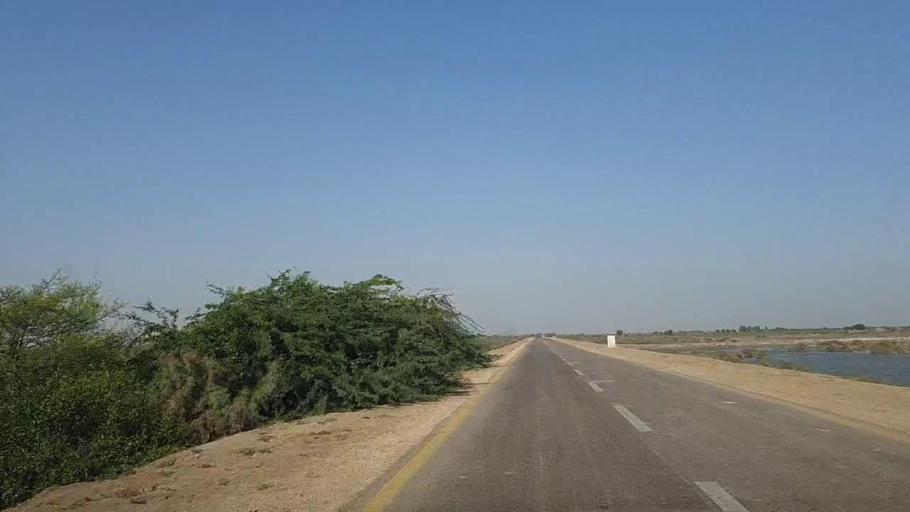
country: PK
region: Sindh
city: Jati
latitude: 24.3988
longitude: 68.2923
